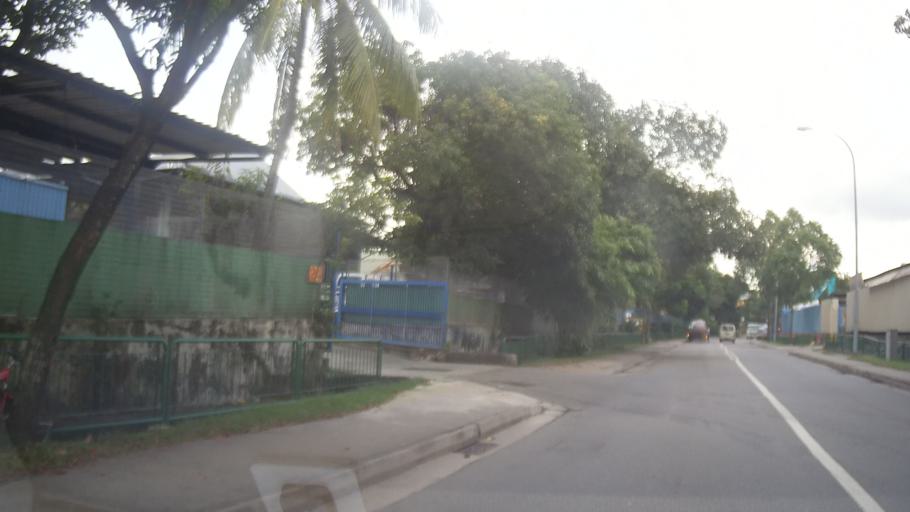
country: MY
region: Johor
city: Johor Bahru
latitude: 1.4212
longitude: 103.7481
